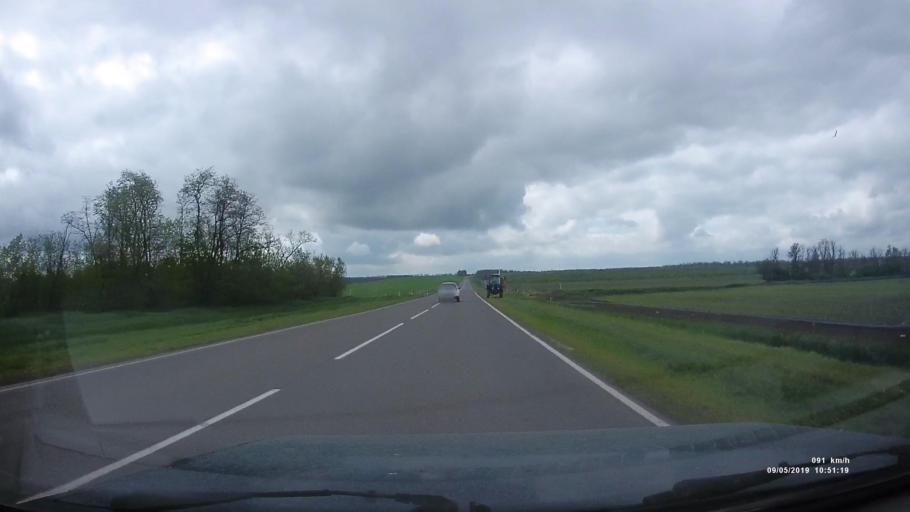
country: RU
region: Rostov
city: Peshkovo
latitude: 46.9164
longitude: 39.3552
